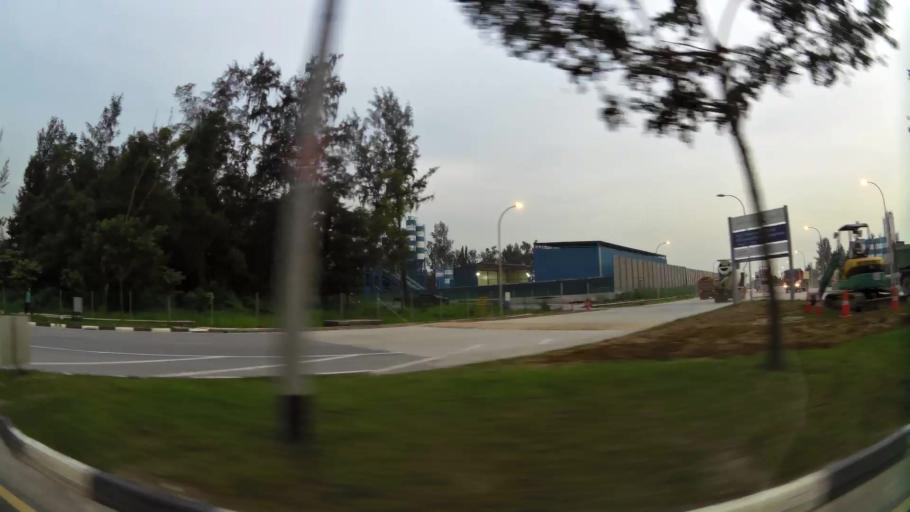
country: SG
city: Singapore
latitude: 1.2927
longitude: 103.8848
